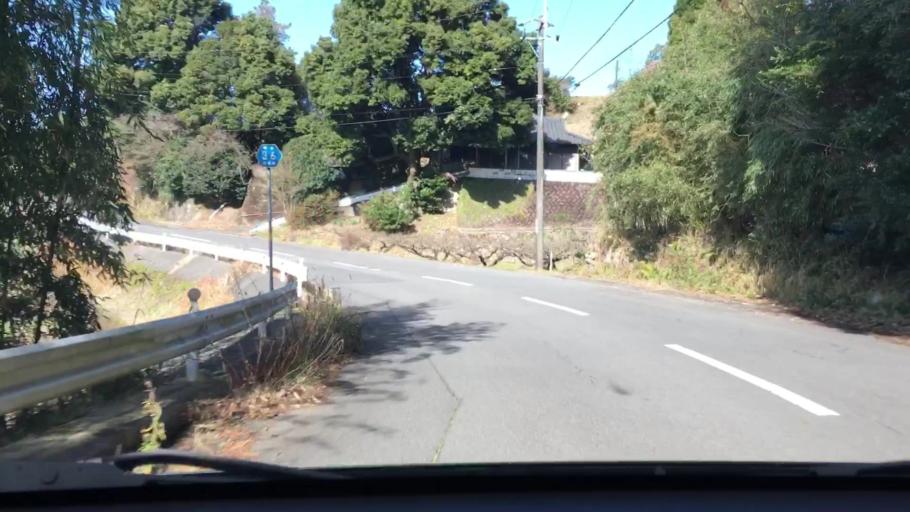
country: JP
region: Kagoshima
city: Ijuin
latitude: 31.7306
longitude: 130.4194
